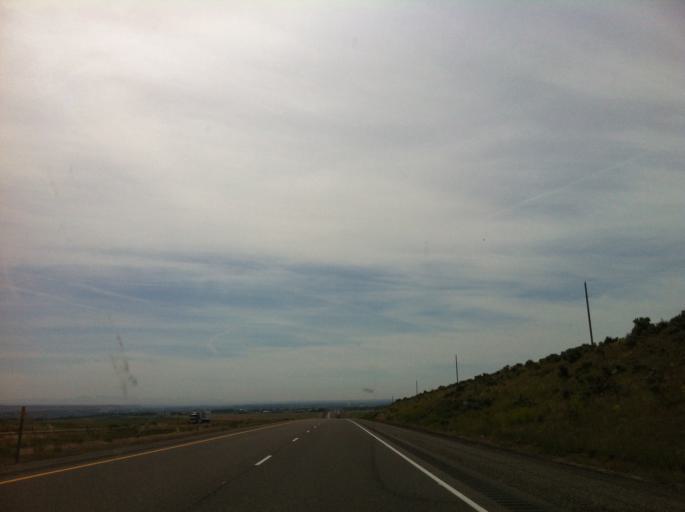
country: US
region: Oregon
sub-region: Malheur County
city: Ontario
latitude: 44.1127
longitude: -117.0578
